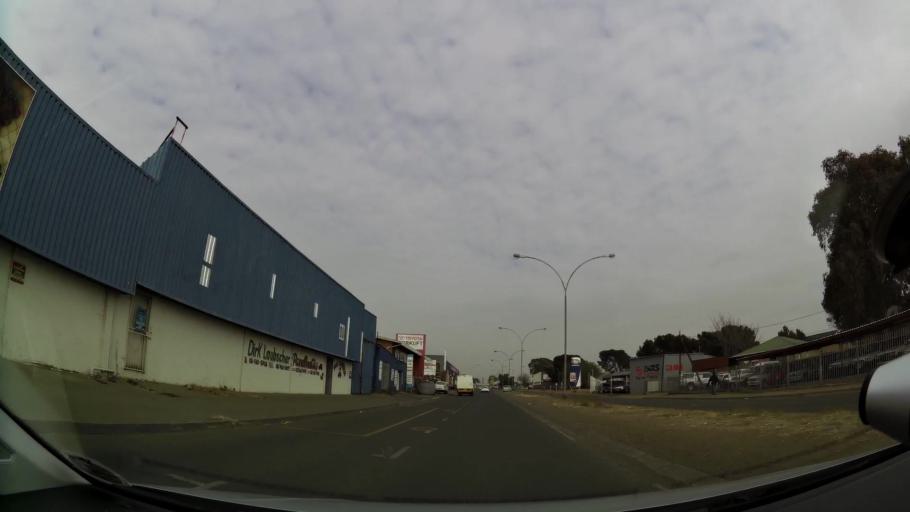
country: ZA
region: Orange Free State
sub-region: Mangaung Metropolitan Municipality
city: Bloemfontein
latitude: -29.1340
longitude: 26.2196
